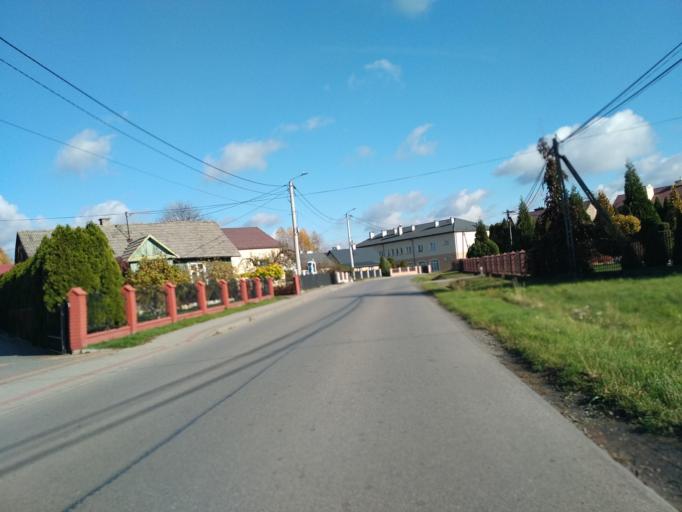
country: PL
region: Subcarpathian Voivodeship
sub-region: Powiat rzeszowski
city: Swilcza
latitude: 50.1163
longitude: 21.8775
